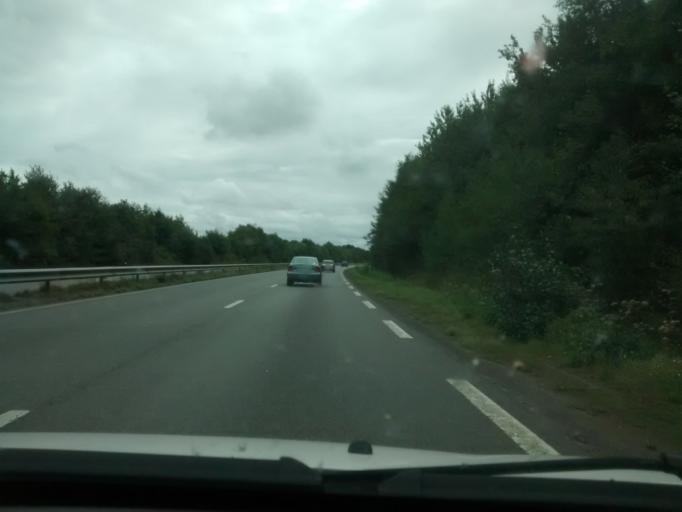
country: FR
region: Brittany
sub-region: Departement d'Ille-et-Vilaine
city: Vignoc
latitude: 48.2715
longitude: -1.7844
